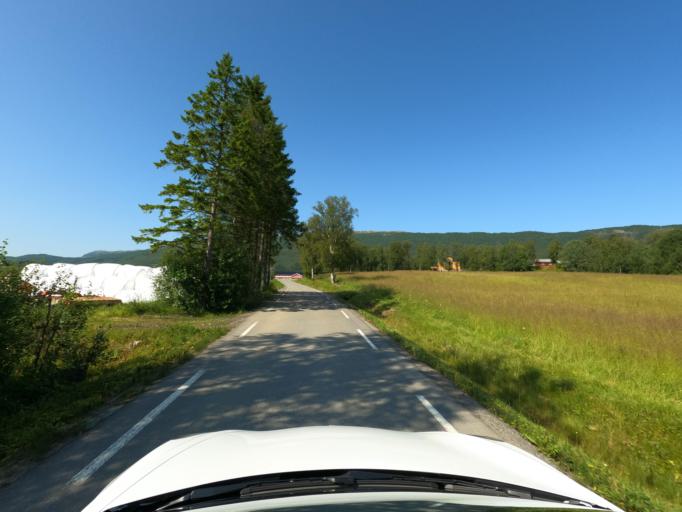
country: NO
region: Nordland
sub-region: Ballangen
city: Ballangen
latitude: 68.3451
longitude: 16.8100
